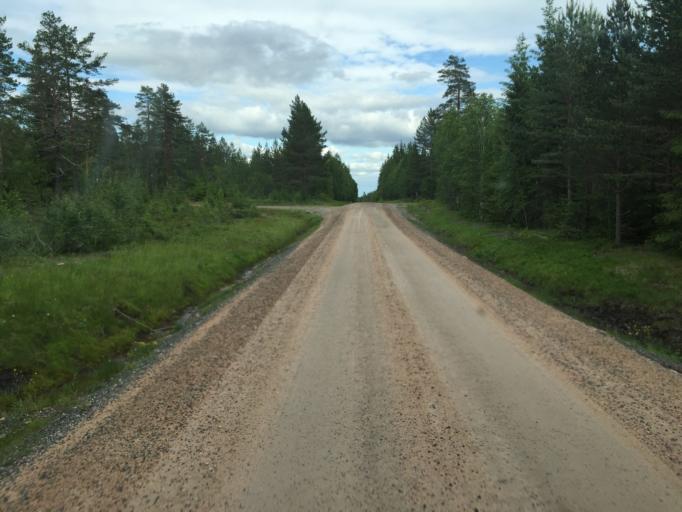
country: SE
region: Dalarna
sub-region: Malung-Saelens kommun
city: Malung
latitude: 60.8950
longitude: 13.7031
